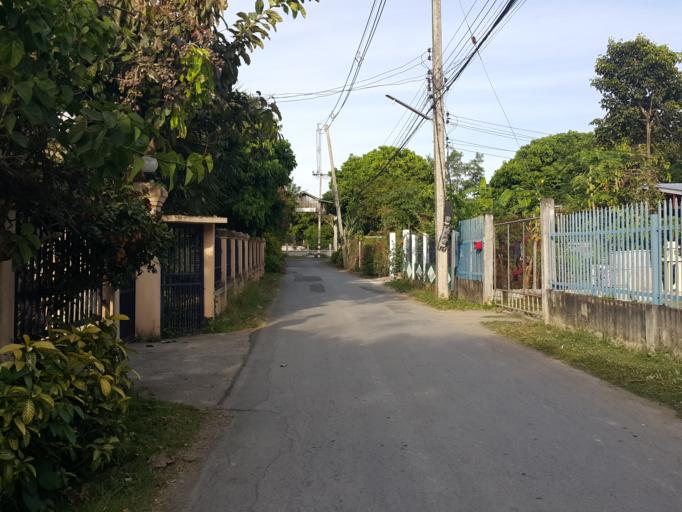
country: TH
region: Chiang Mai
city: San Kamphaeng
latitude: 18.8110
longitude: 99.1291
